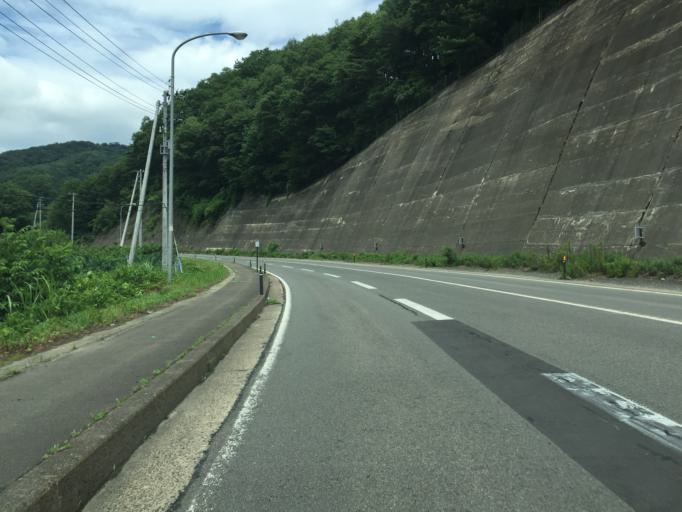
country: JP
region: Fukushima
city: Fukushima-shi
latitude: 37.8339
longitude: 140.3884
